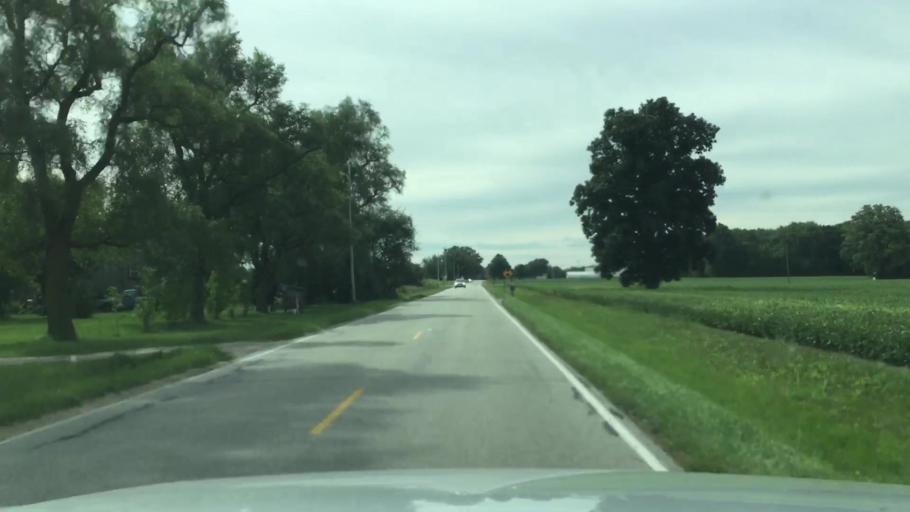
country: US
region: Michigan
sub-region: Genesee County
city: Montrose
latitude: 43.1191
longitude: -83.9880
